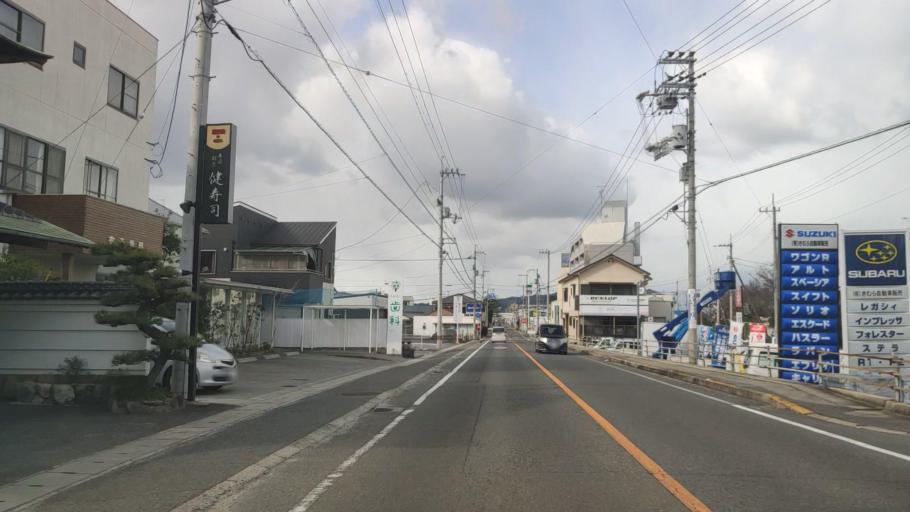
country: JP
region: Ehime
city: Saijo
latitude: 34.0481
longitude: 133.0174
